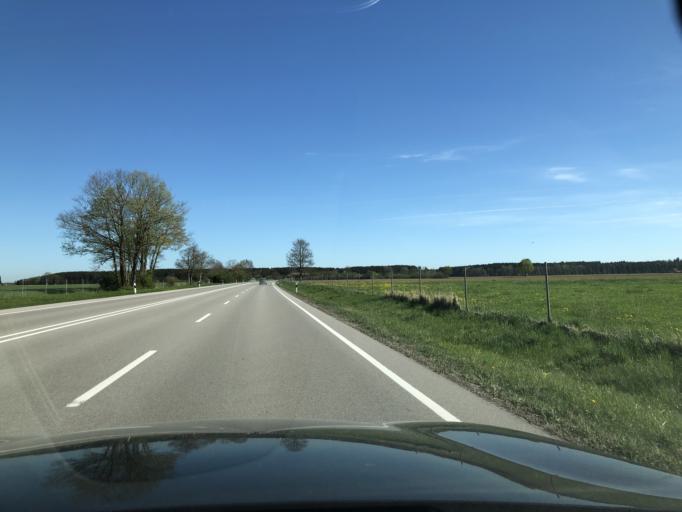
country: DE
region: Bavaria
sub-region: Swabia
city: Rieden
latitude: 47.9699
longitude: 10.6868
